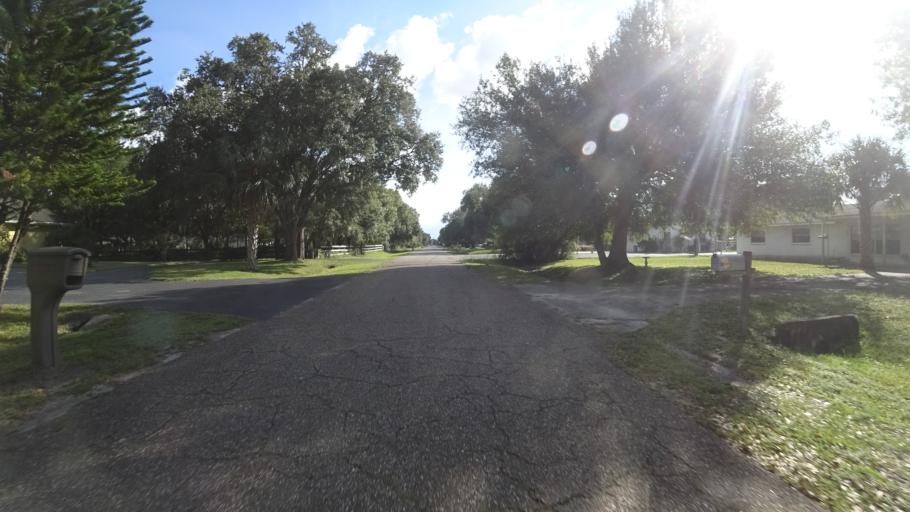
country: US
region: Florida
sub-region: Manatee County
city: Ellenton
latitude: 27.4887
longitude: -82.4753
